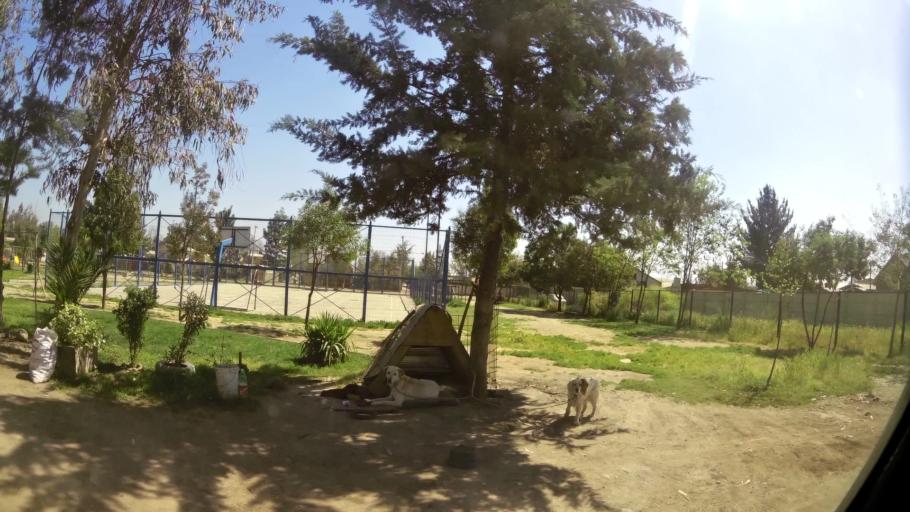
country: CL
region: Santiago Metropolitan
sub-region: Provincia de Talagante
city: Penaflor
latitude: -33.5866
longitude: -70.8054
